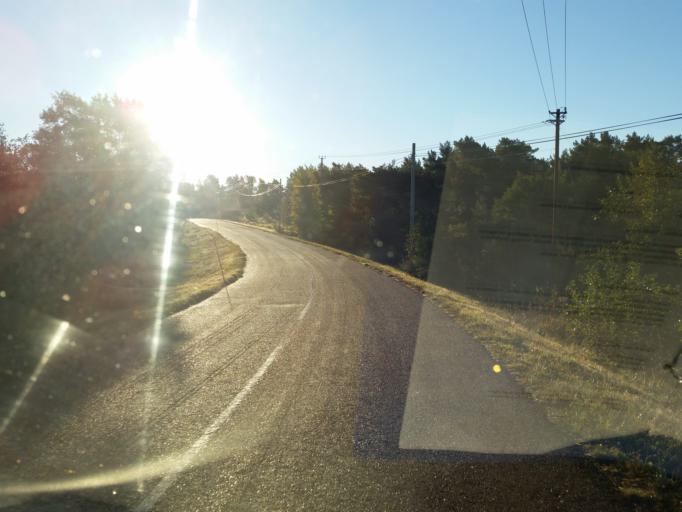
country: AX
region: Alands skaergard
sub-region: Vardoe
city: Vardoe
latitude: 60.3097
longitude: 20.3764
